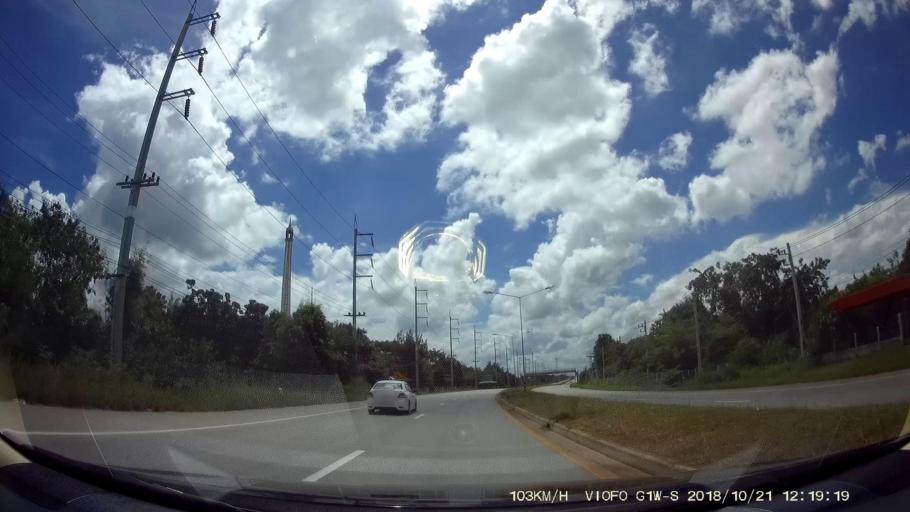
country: TH
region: Nakhon Ratchasima
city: Dan Khun Thot
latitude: 15.3025
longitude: 101.8143
